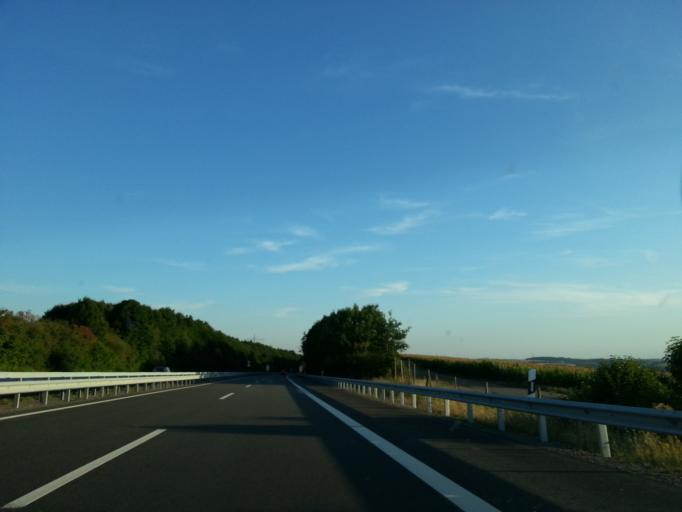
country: DE
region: Rheinland-Pfalz
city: Hoheinod
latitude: 49.2818
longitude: 7.6128
